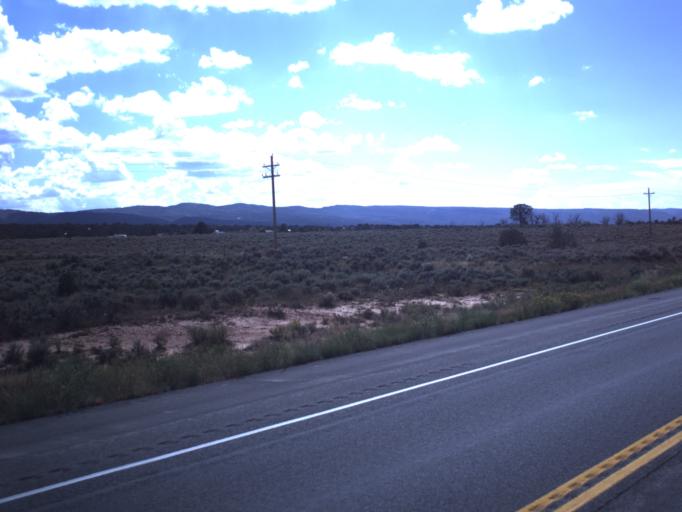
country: US
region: Utah
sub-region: Duchesne County
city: Duchesne
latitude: 40.2048
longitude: -110.7234
